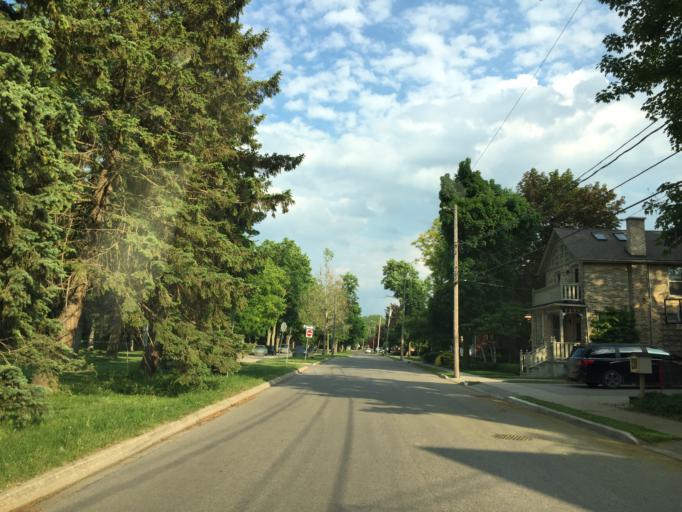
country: CA
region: Ontario
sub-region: Wellington County
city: Guelph
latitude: 43.5489
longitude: -80.2633
